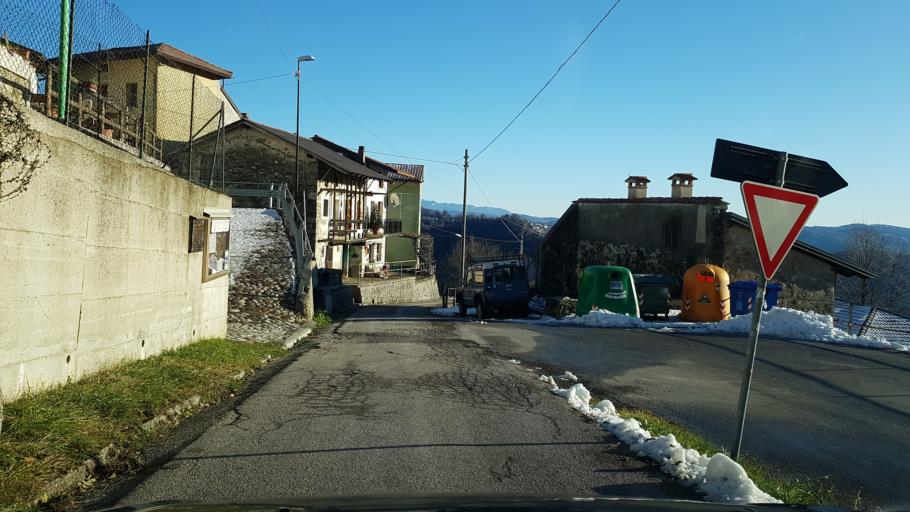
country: IT
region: Friuli Venezia Giulia
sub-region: Provincia di Udine
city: Savogna
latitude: 46.1873
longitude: 13.5321
